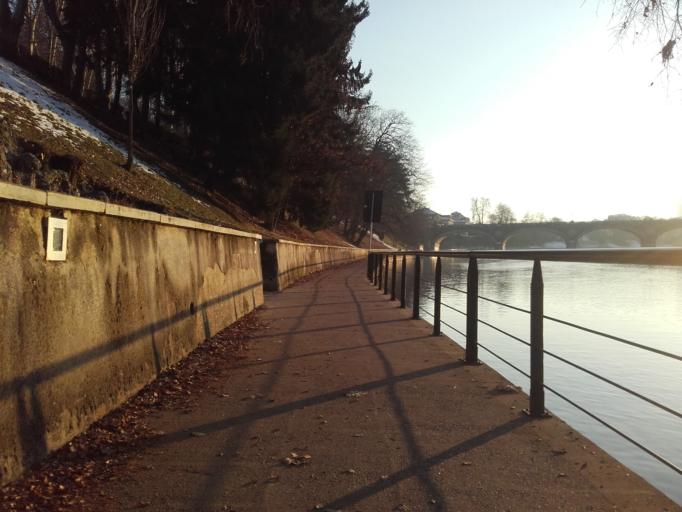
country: IT
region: Piedmont
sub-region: Provincia di Torino
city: Turin
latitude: 45.0470
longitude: 7.6866
